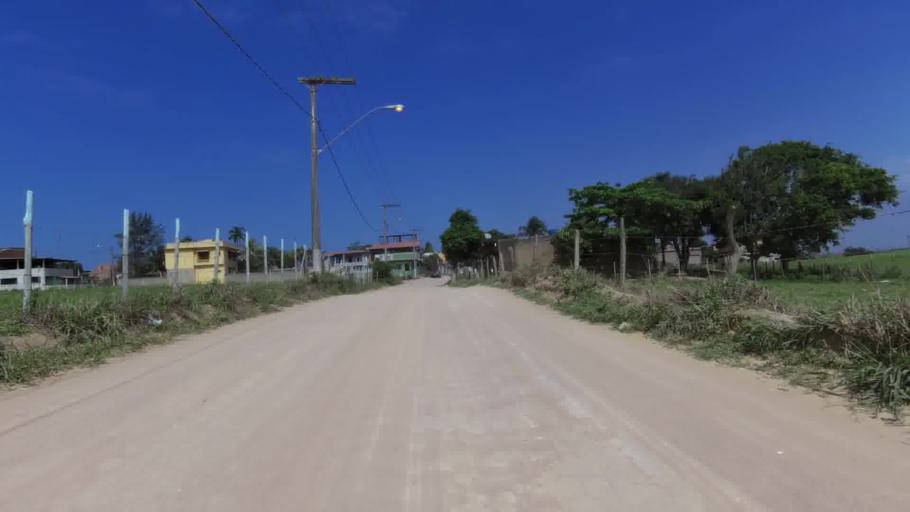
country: BR
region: Espirito Santo
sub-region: Marataizes
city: Marataizes
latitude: -21.0275
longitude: -40.8209
